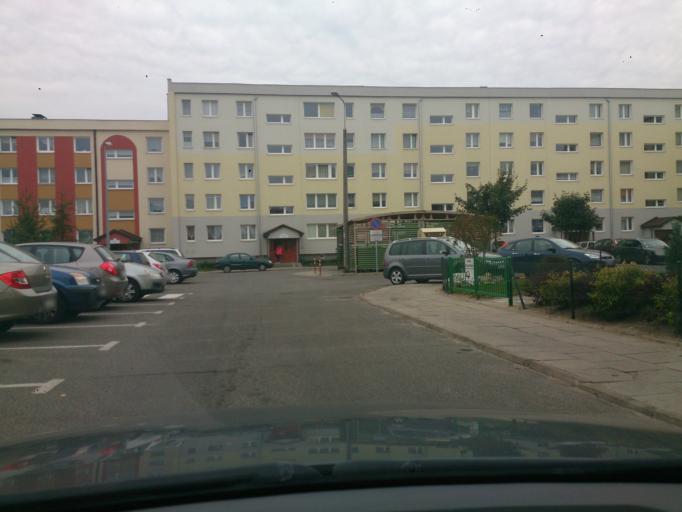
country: PL
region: Pomeranian Voivodeship
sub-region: Powiat wejherowski
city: Reda
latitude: 54.6016
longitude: 18.3567
